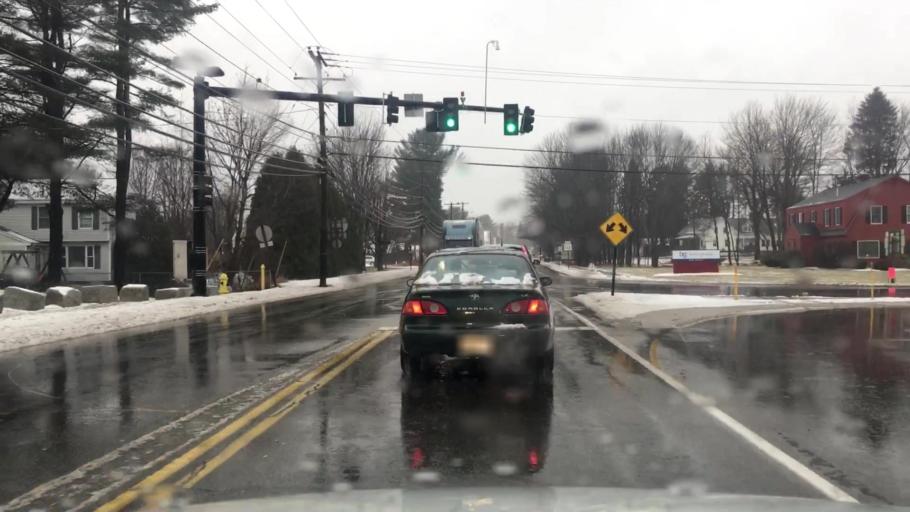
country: US
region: Maine
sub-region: York County
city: Saco
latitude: 43.5157
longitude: -70.4531
